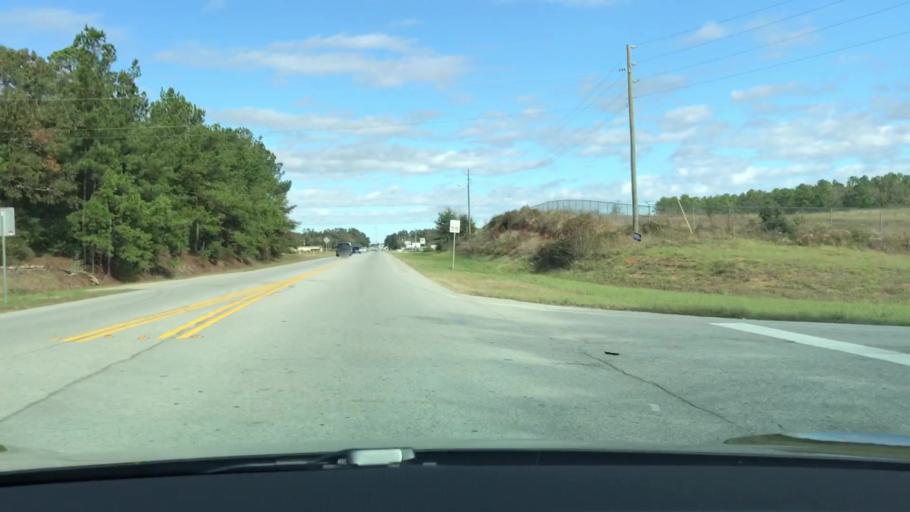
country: US
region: Georgia
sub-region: Jefferson County
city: Louisville
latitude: 32.9883
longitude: -82.3928
